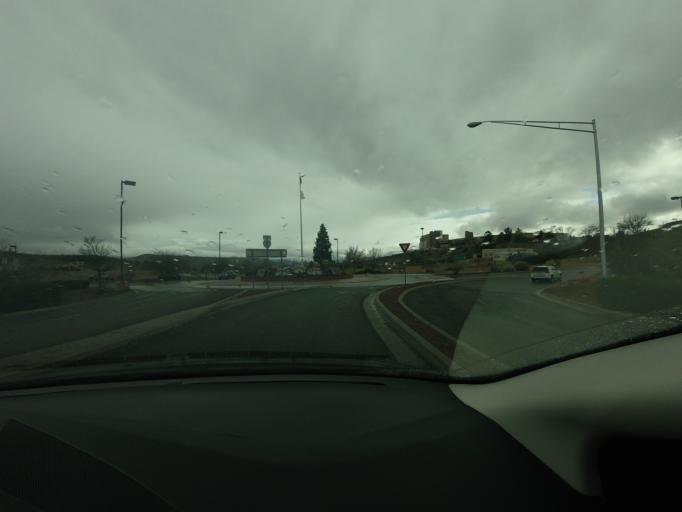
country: US
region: Arizona
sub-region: Yavapai County
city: Camp Verde
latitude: 34.6096
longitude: -111.8615
